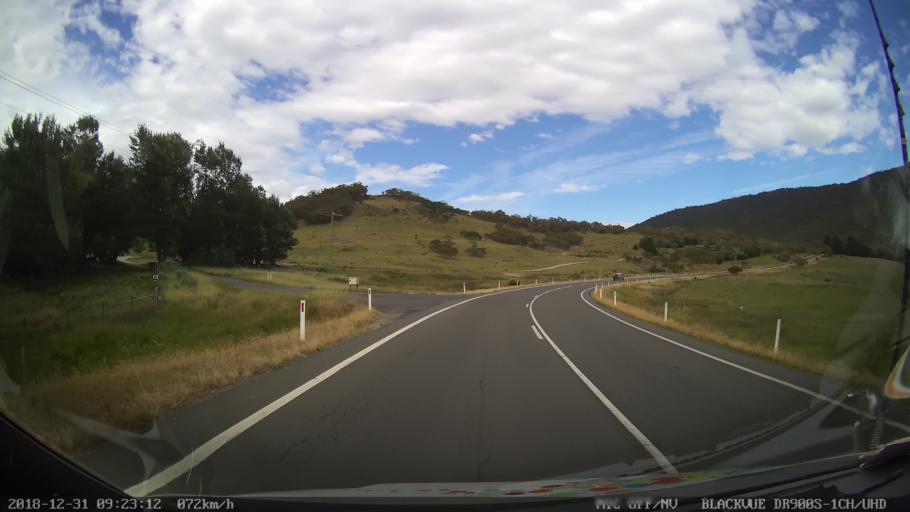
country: AU
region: New South Wales
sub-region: Snowy River
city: Jindabyne
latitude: -36.4377
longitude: 148.5369
